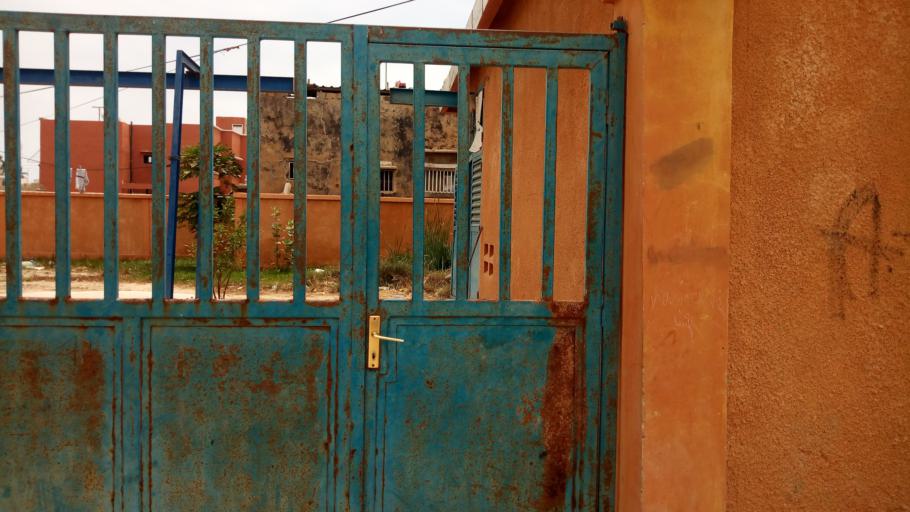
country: SN
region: Saint-Louis
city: Saint-Louis
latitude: 16.0155
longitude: -16.4860
